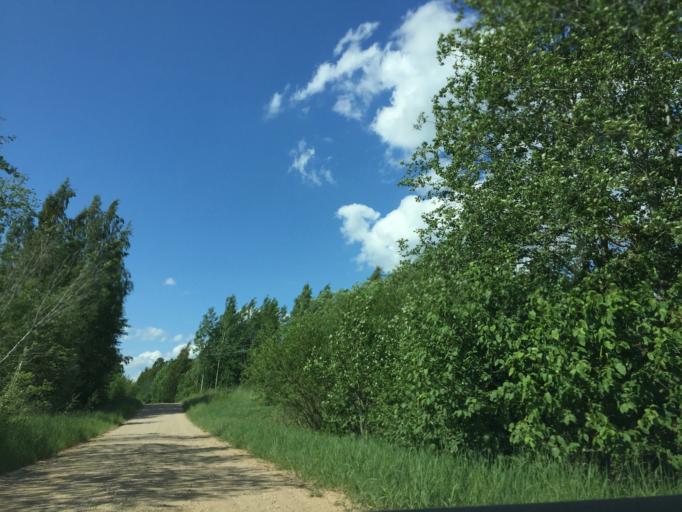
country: LV
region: Priekuli
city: Priekuli
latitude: 57.2554
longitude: 25.3900
